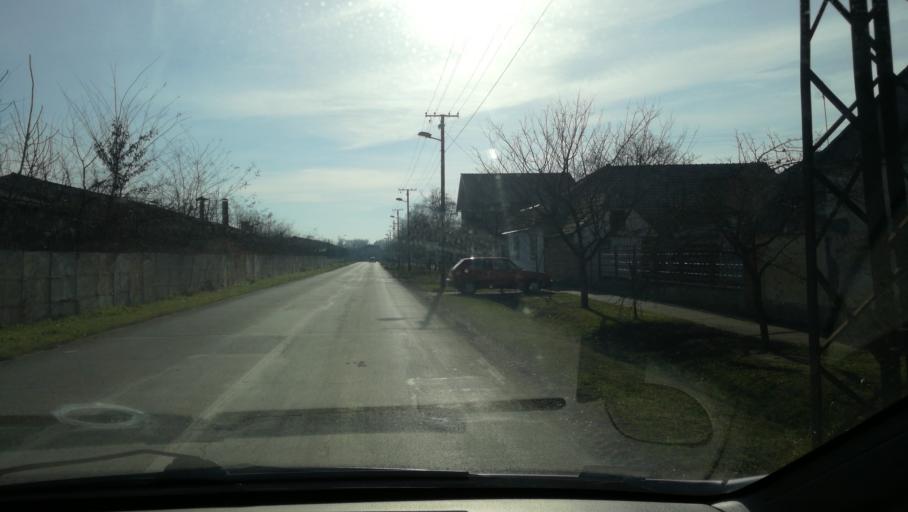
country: RS
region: Autonomna Pokrajina Vojvodina
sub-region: Severnobanatski Okrug
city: Kikinda
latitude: 45.8362
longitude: 20.4892
